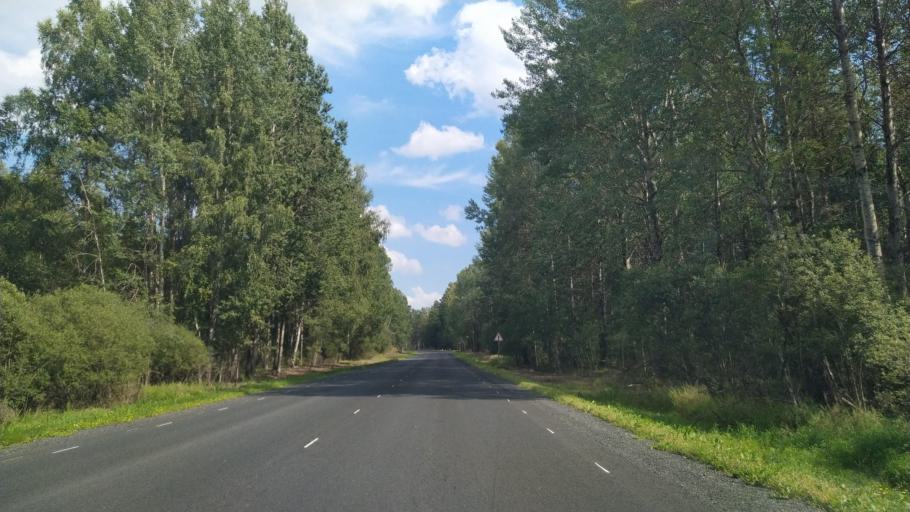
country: RU
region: Pskov
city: Porkhov
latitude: 57.7173
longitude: 29.2131
